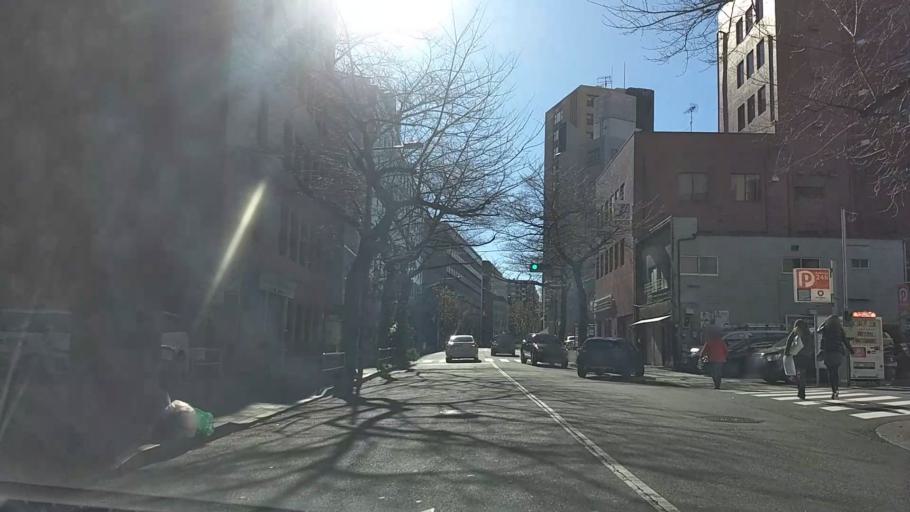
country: JP
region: Tokyo
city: Tokyo
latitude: 35.6928
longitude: 139.7439
